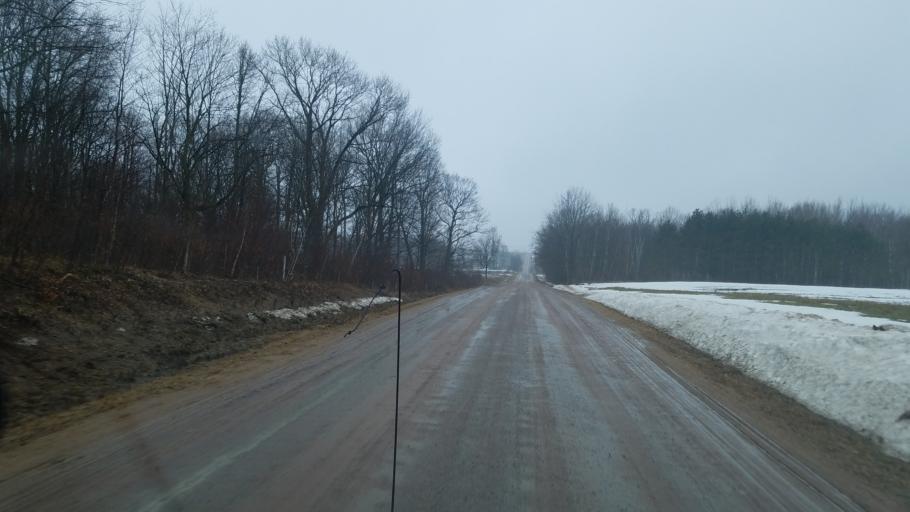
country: US
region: Wisconsin
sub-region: Clark County
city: Loyal
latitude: 44.6095
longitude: -90.3969
